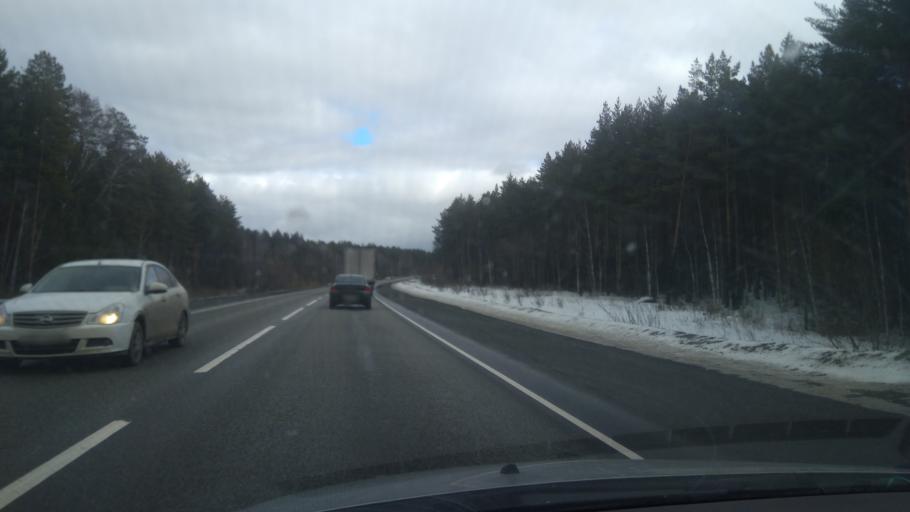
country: RU
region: Sverdlovsk
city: Bisert'
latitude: 56.8291
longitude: 58.7753
